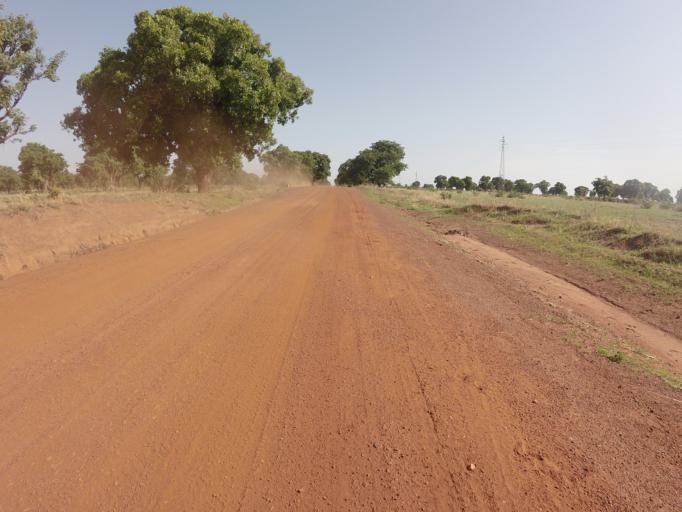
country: GH
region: Upper East
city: Bawku
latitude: 10.7729
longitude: -0.1941
